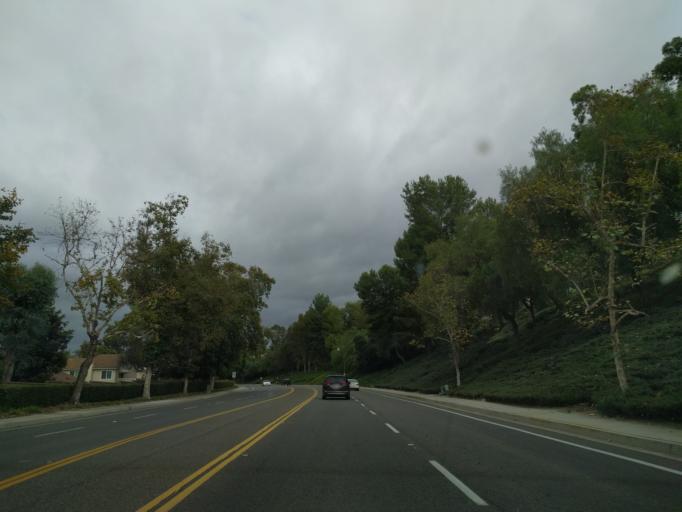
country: US
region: California
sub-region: Orange County
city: Mission Viejo
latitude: 33.5977
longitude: -117.6493
